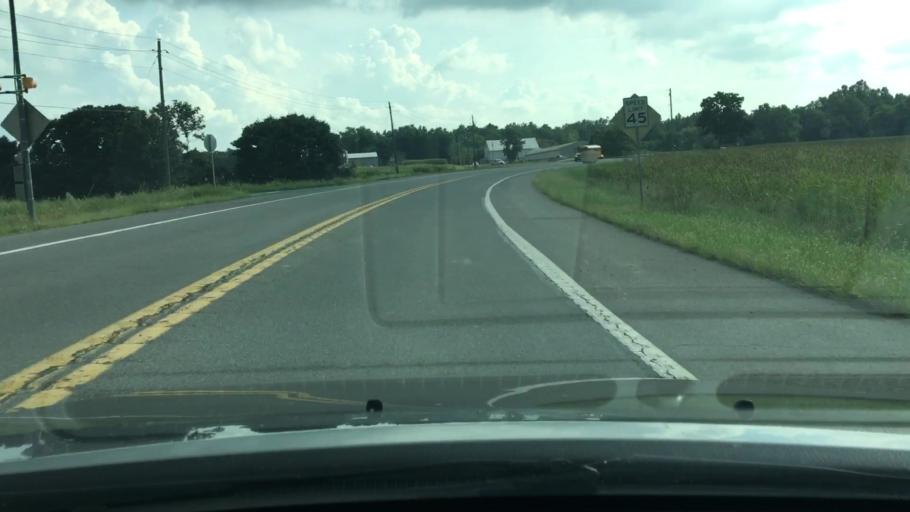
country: US
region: Pennsylvania
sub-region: Franklin County
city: Scotland
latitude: 39.9430
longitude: -77.5831
